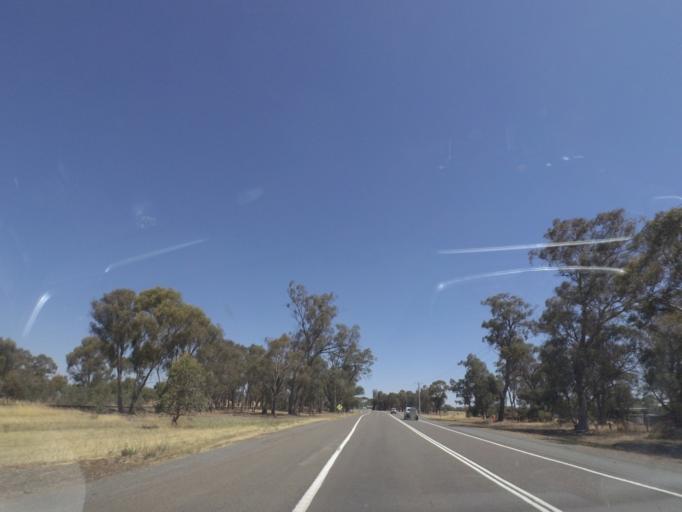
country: AU
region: Victoria
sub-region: Greater Shepparton
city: Shepparton
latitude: -36.2351
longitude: 145.4317
